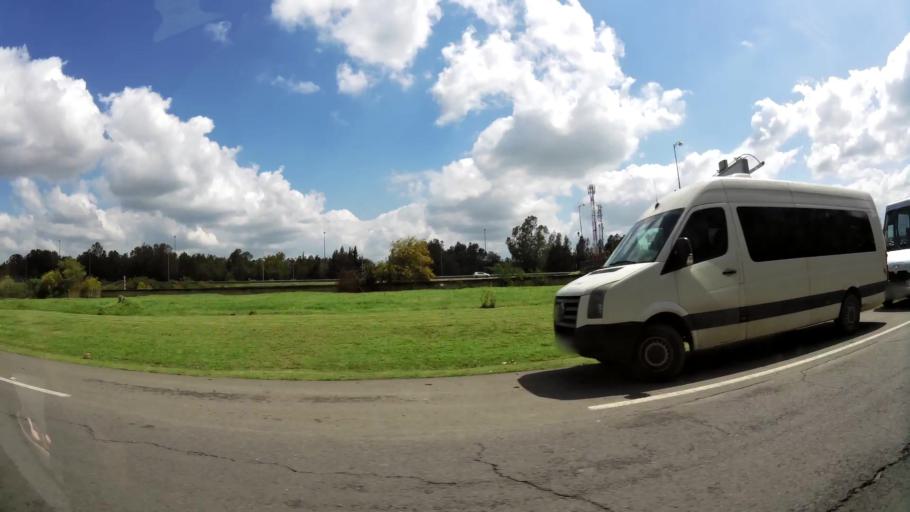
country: MA
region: Chaouia-Ouardigha
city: Nouaseur
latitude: 33.3752
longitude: -7.5762
